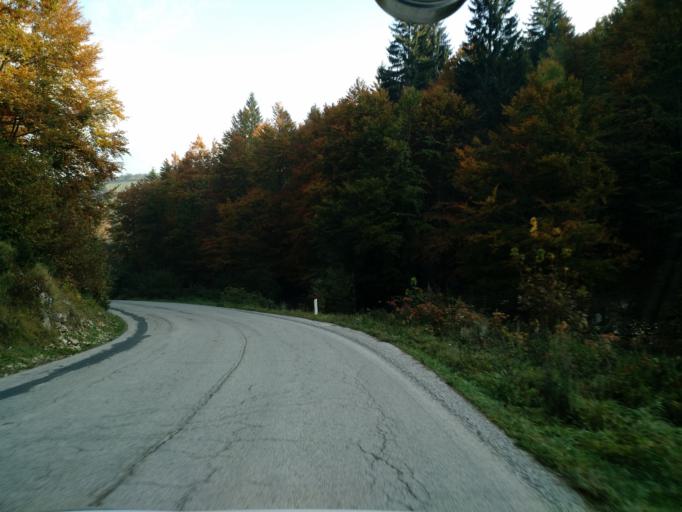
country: IT
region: Veneto
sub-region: Provincia di Vicenza
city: Foza
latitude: 45.8580
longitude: 11.6093
